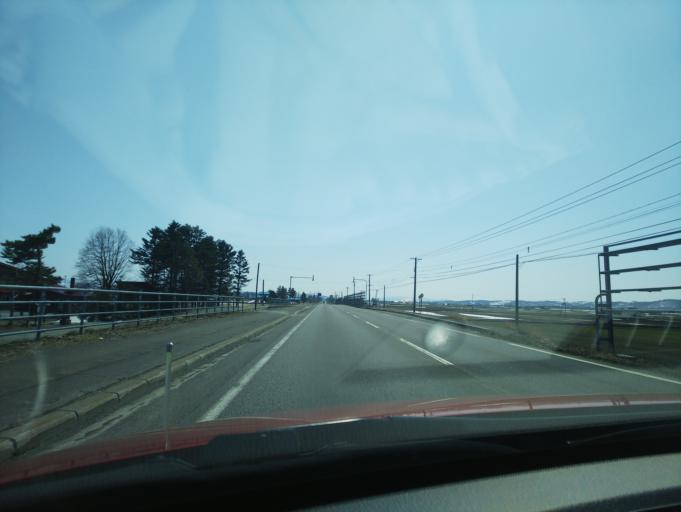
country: JP
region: Hokkaido
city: Nayoro
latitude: 44.2204
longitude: 142.3949
